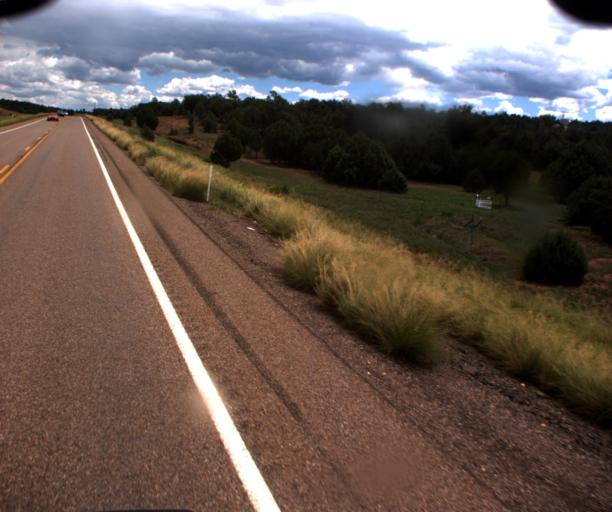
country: US
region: Arizona
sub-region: Navajo County
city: Linden
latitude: 34.3460
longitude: -110.2971
